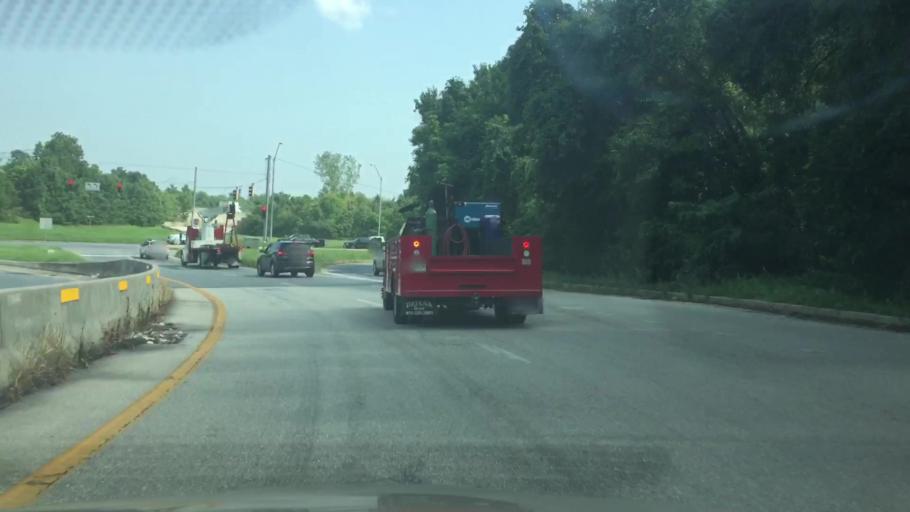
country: US
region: Maryland
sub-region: Anne Arundel County
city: South Gate
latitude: 39.1273
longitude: -76.6428
